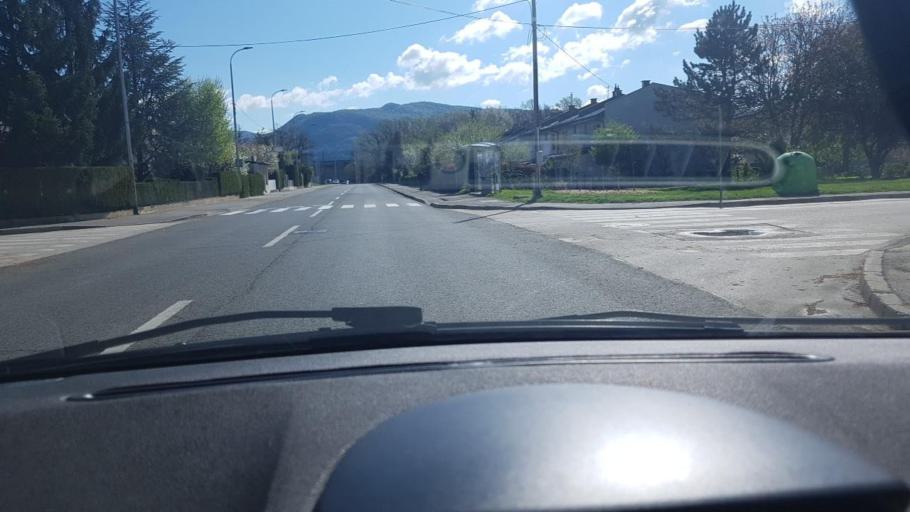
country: HR
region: Zagrebacka
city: Zapresic
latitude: 45.8695
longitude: 15.7999
